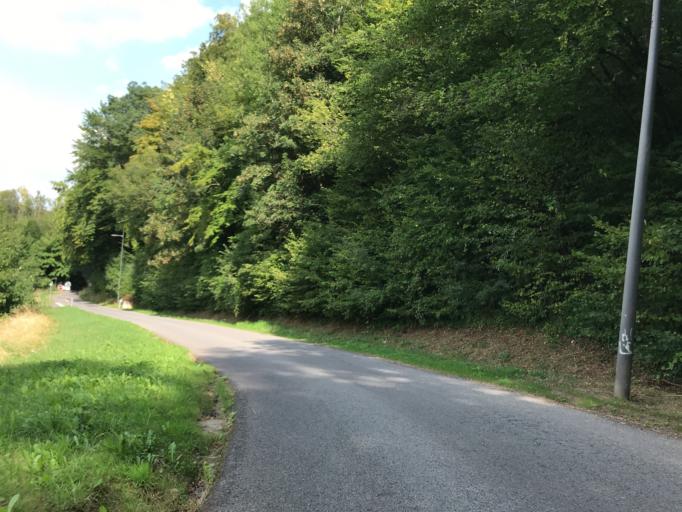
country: FR
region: Lorraine
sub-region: Departement de Meurthe-et-Moselle
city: Thil
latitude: 49.4920
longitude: 5.9128
